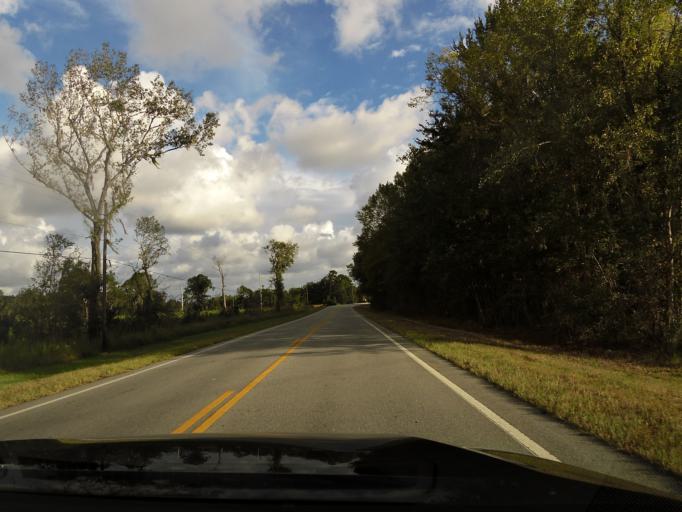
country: US
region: Georgia
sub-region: Liberty County
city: Midway
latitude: 31.7535
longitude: -81.4417
